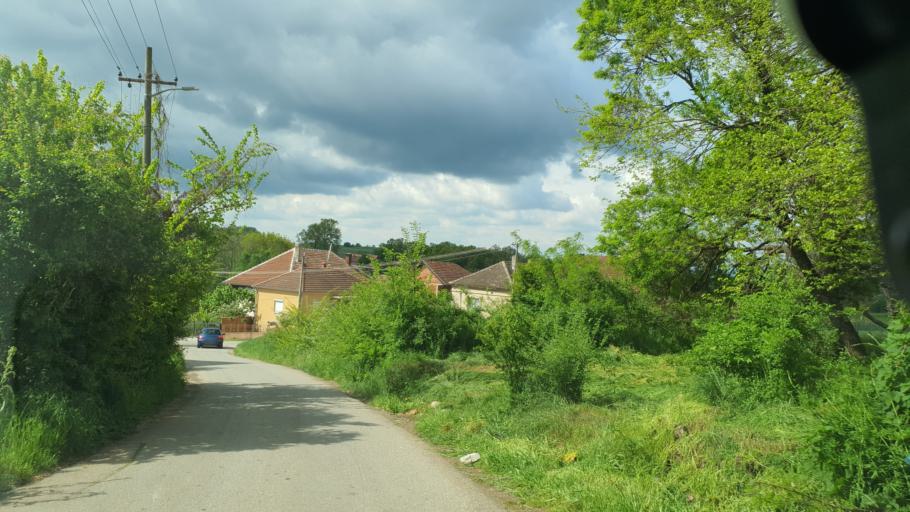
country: RS
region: Central Serbia
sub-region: Pomoravski Okrug
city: Paracin
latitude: 43.9375
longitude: 21.4931
